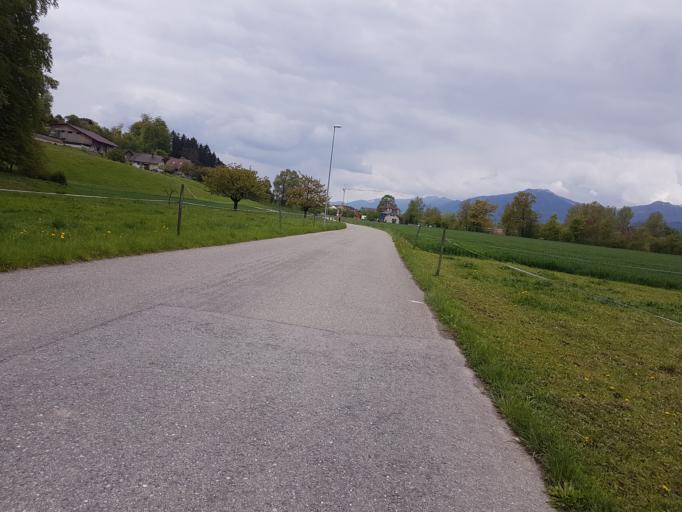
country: CH
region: Bern
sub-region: Oberaargau
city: Wangen an der Aare
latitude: 47.2348
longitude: 7.6682
